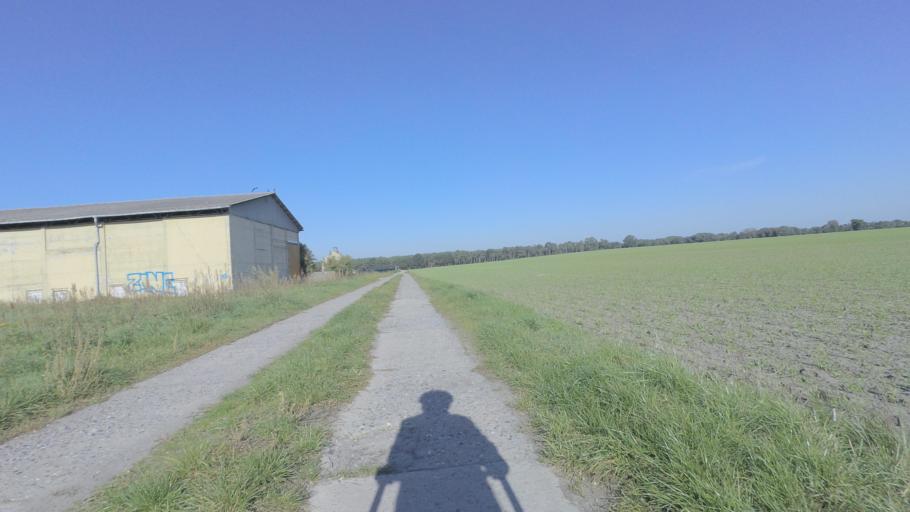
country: DE
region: Brandenburg
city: Rangsdorf
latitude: 52.2753
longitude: 13.3499
